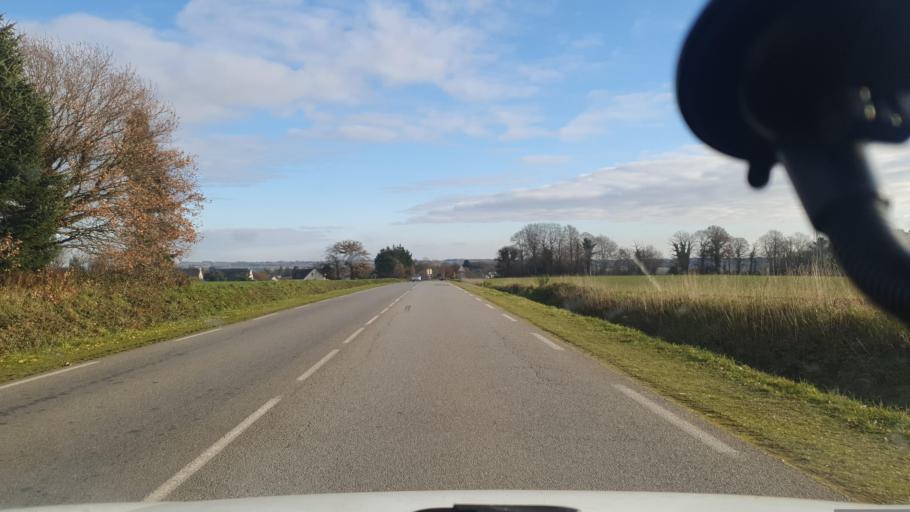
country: FR
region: Brittany
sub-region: Departement du Finistere
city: Briec
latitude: 48.0987
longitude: -4.0124
